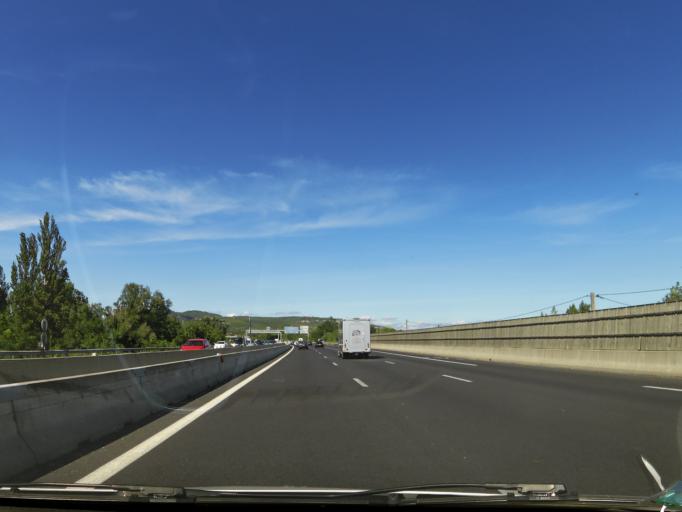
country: FR
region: Provence-Alpes-Cote d'Azur
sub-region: Departement du Vaucluse
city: Bollene
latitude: 44.2882
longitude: 4.7415
